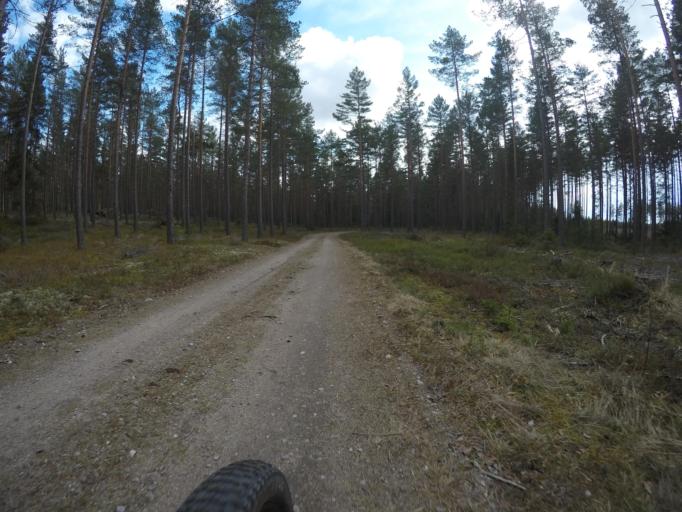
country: SE
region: Vaestmanland
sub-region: Kungsors Kommun
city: Kungsoer
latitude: 59.3381
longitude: 16.1069
